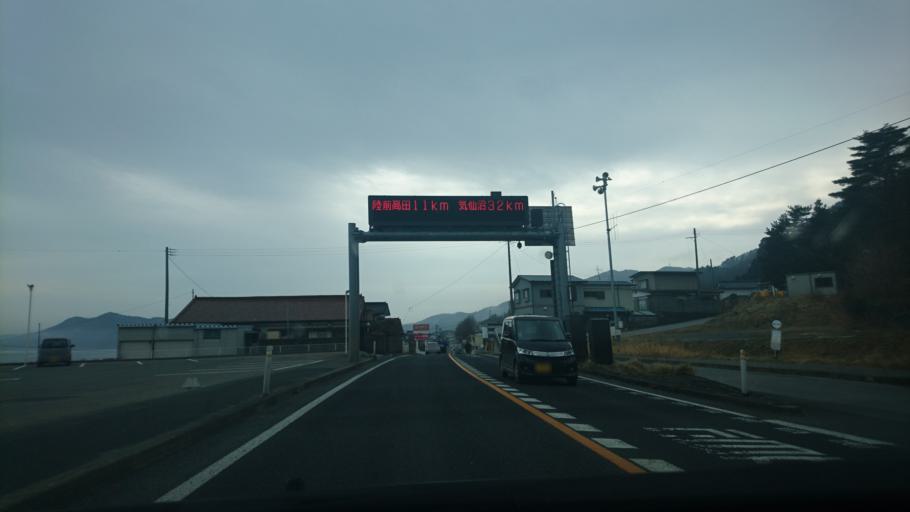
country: JP
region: Iwate
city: Ofunato
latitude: 39.0418
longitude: 141.7218
